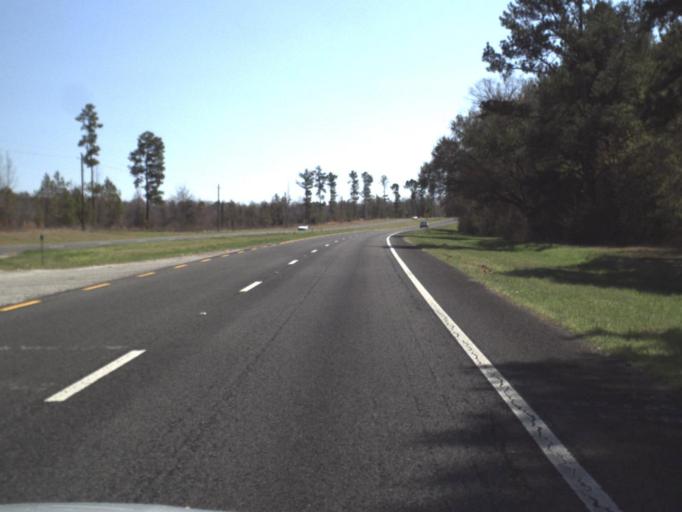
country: US
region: Florida
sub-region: Jackson County
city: Graceville
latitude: 30.9620
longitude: -85.4049
